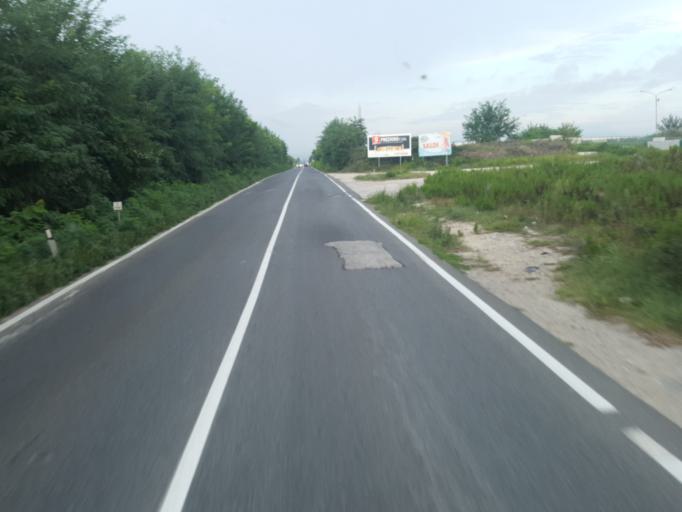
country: IT
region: Campania
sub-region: Provincia di Caserta
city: Pignataro Maggiore
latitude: 41.1682
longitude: 14.1512
